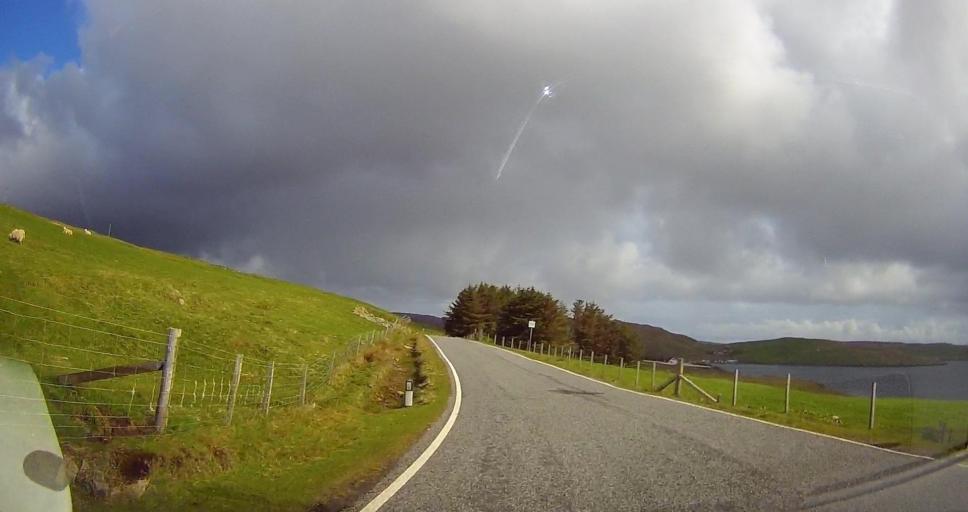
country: GB
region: Scotland
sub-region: Shetland Islands
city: Lerwick
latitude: 60.5307
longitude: -1.3633
